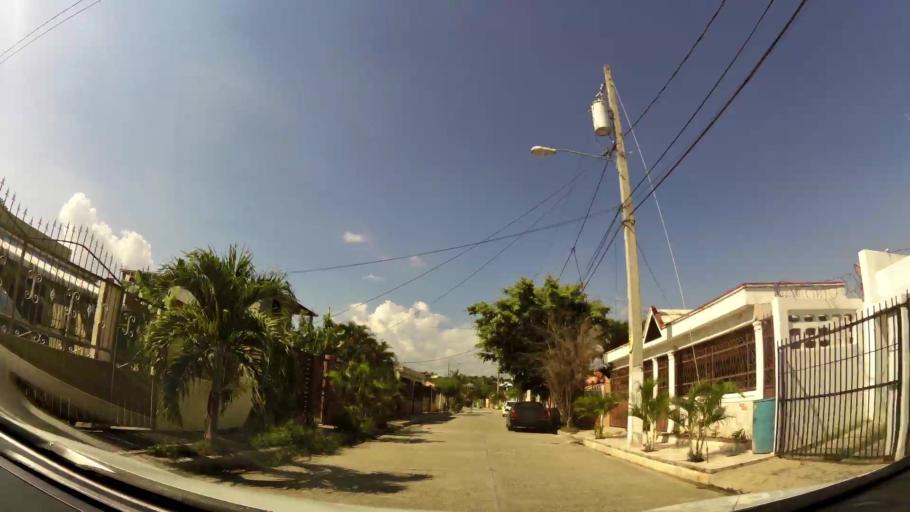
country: DO
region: San Cristobal
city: El Carril
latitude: 18.4709
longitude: -70.0083
